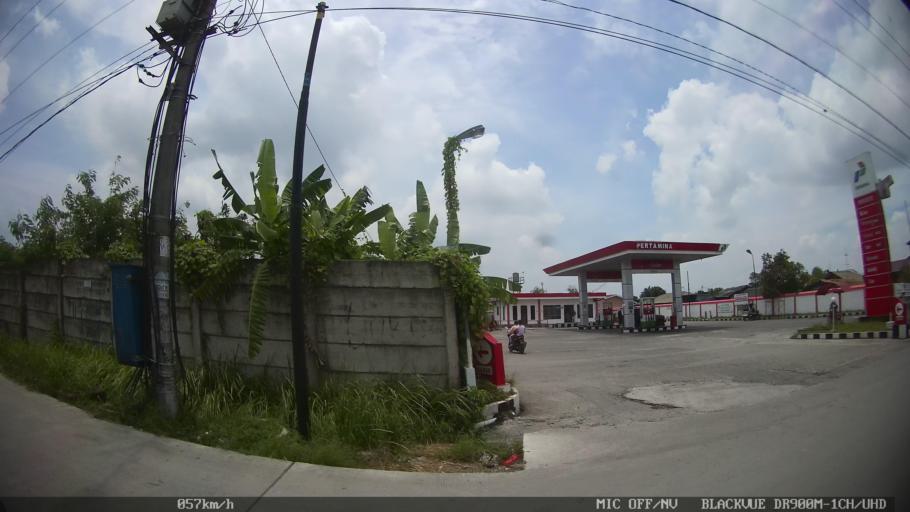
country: ID
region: North Sumatra
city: Labuhan Deli
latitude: 3.6934
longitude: 98.6785
